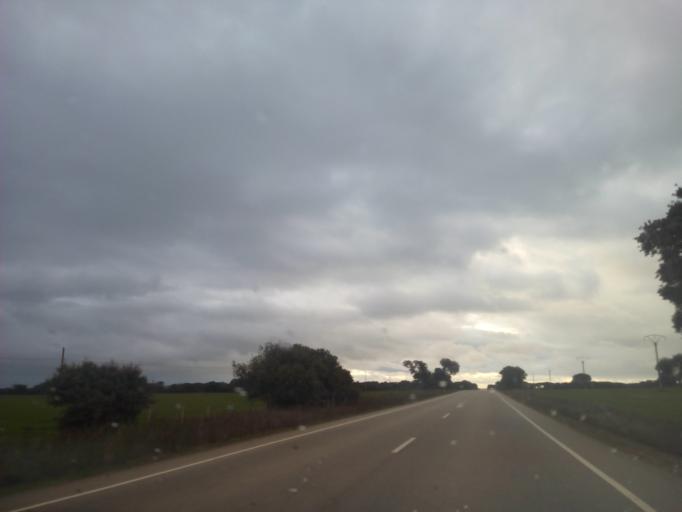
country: ES
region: Castille and Leon
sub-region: Provincia de Salamanca
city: Cabrillas
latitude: 40.7577
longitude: -6.1945
